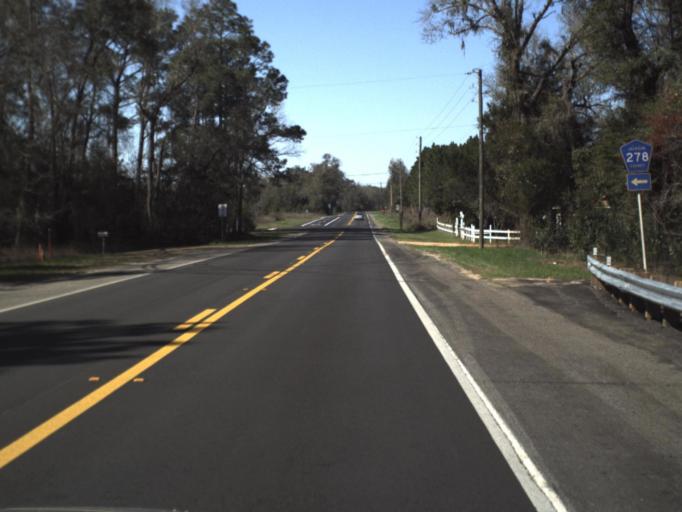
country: US
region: Florida
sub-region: Jackson County
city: Marianna
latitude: 30.6252
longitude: -85.1531
